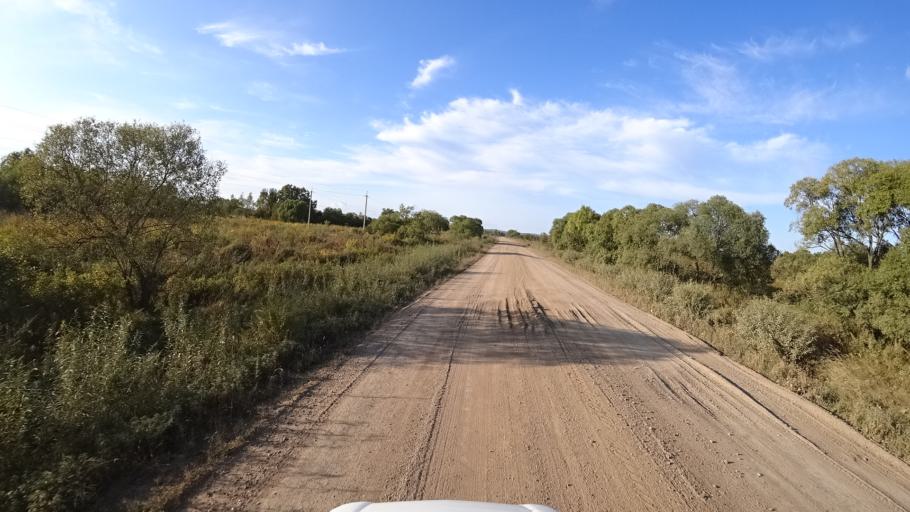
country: RU
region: Amur
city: Arkhara
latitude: 49.3569
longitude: 130.1373
